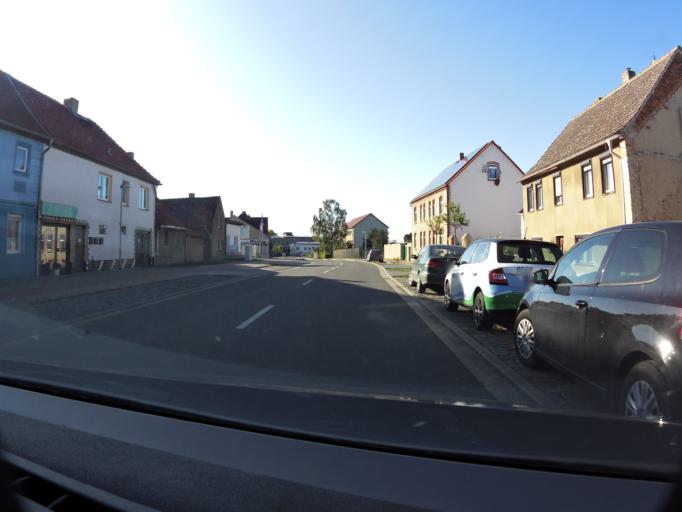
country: DE
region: Saxony-Anhalt
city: Groeningen
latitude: 51.9425
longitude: 11.2167
